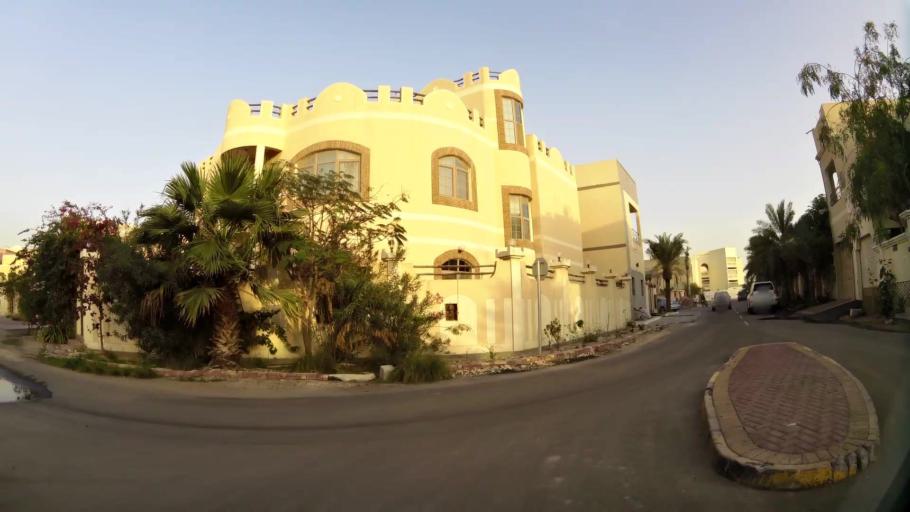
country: BH
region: Northern
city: Madinat `Isa
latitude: 26.1875
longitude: 50.4767
